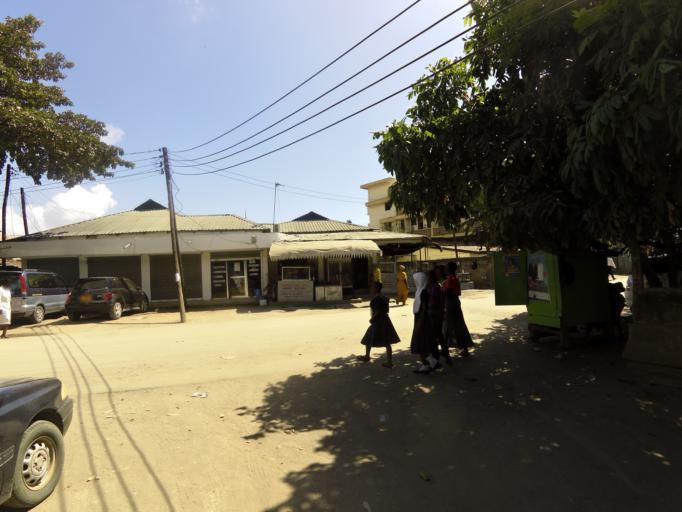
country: TZ
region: Dar es Salaam
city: Magomeni
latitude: -6.7874
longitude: 39.2615
